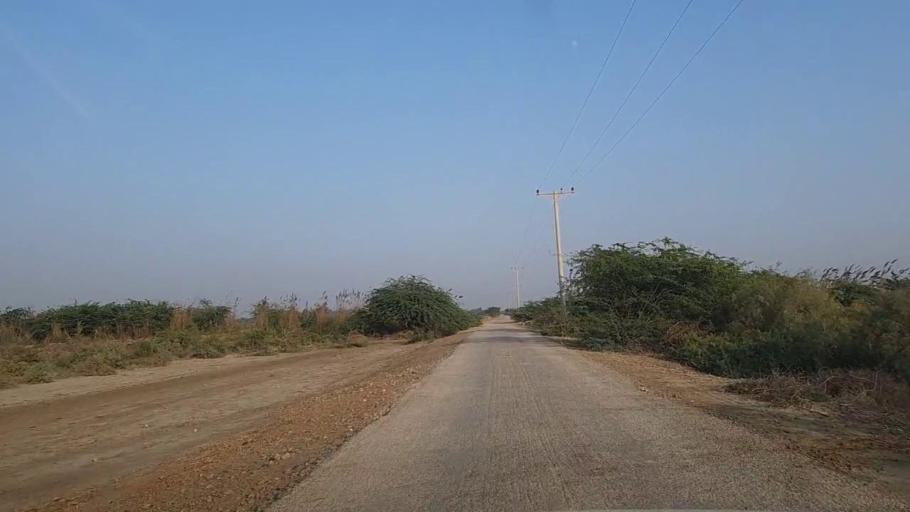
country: PK
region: Sindh
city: Keti Bandar
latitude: 24.2805
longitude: 67.6173
